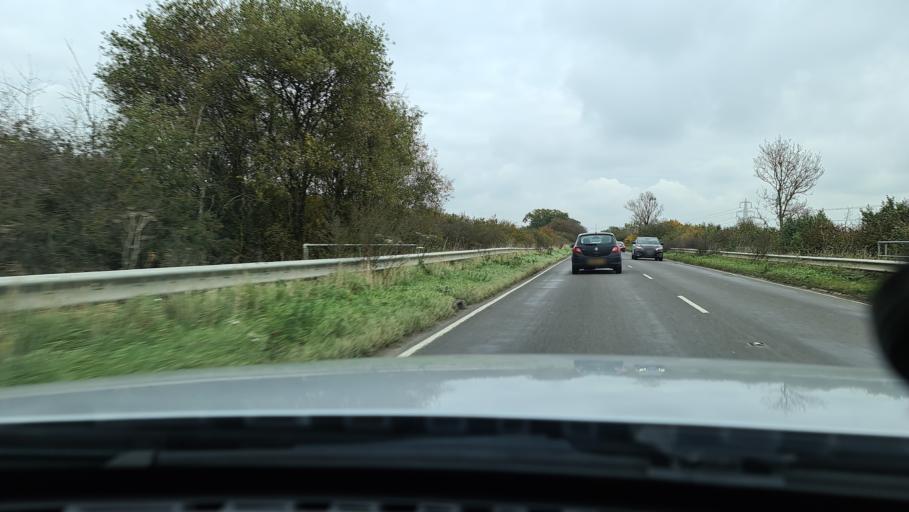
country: GB
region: England
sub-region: Buckinghamshire
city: Steeple Claydon
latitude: 51.8723
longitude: -1.0442
